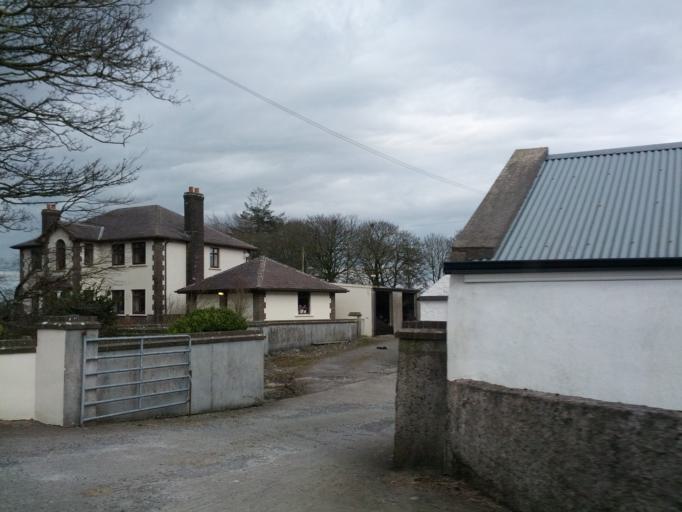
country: IE
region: Connaught
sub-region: County Galway
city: Athenry
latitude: 53.4495
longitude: -8.6333
